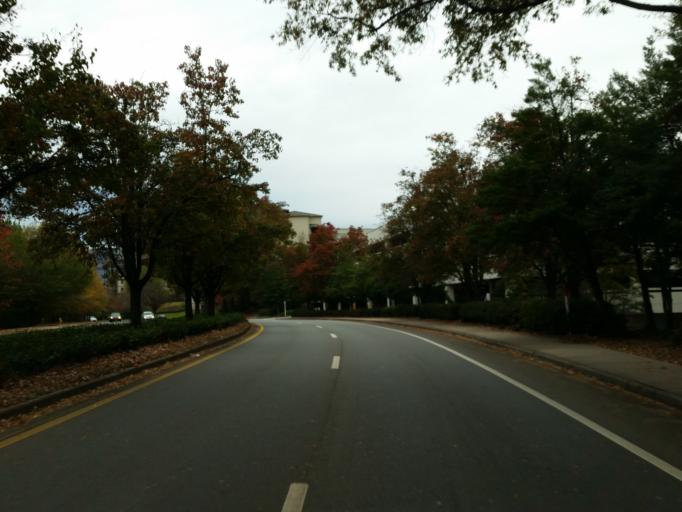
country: US
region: Georgia
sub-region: DeKalb County
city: Dunwoody
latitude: 33.9318
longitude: -84.3403
